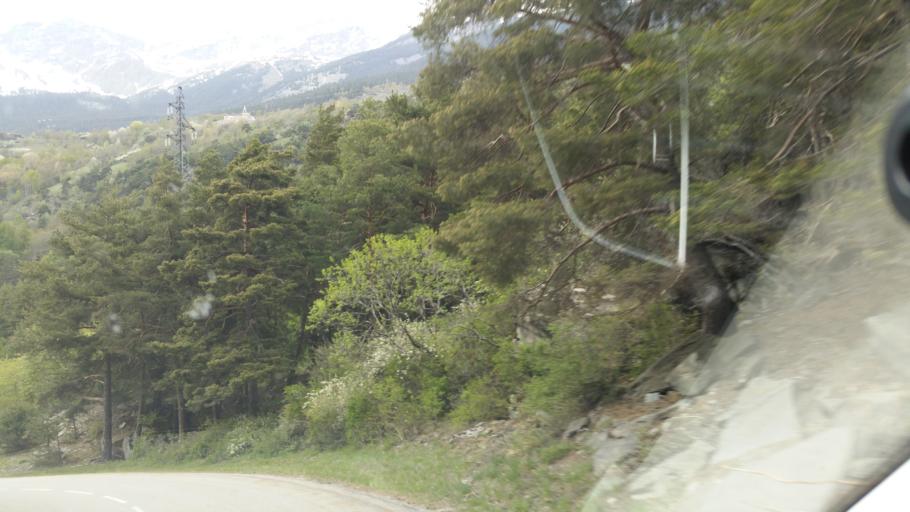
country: FR
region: Rhone-Alpes
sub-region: Departement de la Savoie
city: Modane
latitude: 45.2010
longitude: 6.6039
